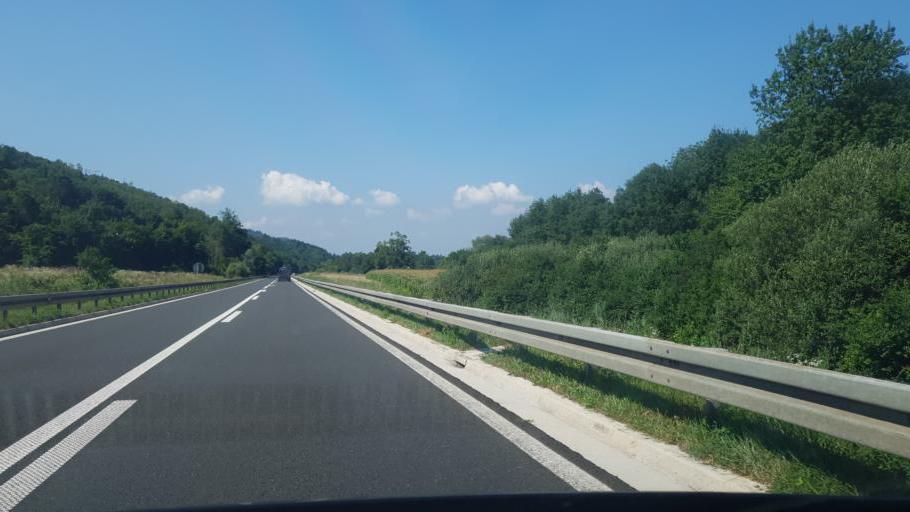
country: HR
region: Istarska
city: Pazin
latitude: 45.2987
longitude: 14.0478
